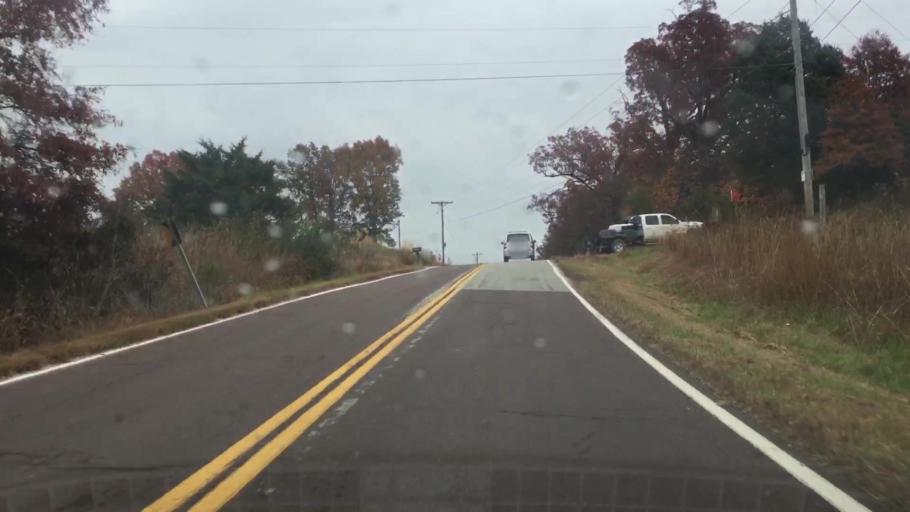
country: US
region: Missouri
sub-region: Callaway County
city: Fulton
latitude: 38.7879
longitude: -91.7885
